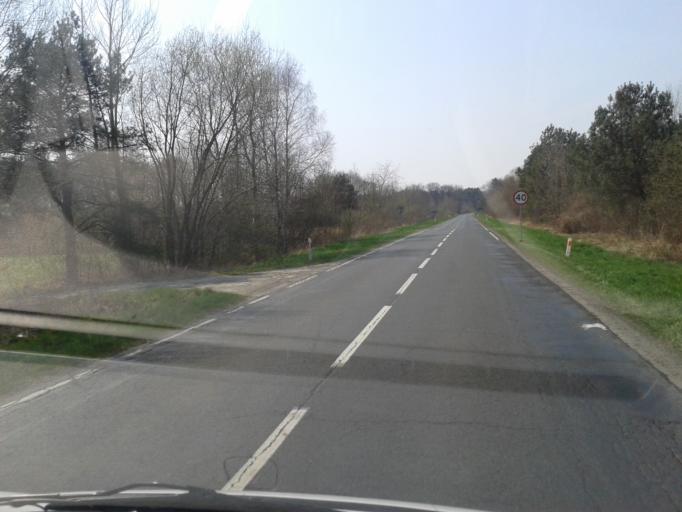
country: PL
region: Subcarpathian Voivodeship
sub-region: Powiat jaroslawski
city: Laszki
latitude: 50.0755
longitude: 22.8372
